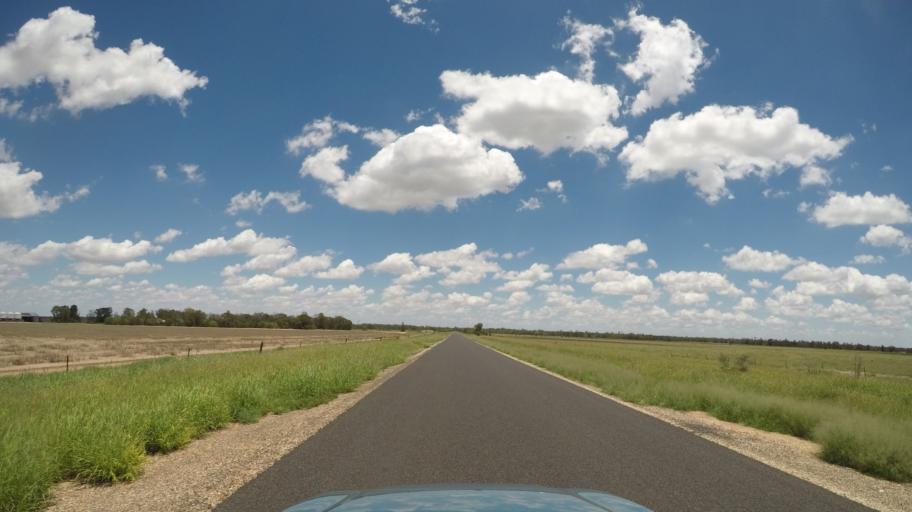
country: AU
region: Queensland
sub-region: Goondiwindi
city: Goondiwindi
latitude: -28.1610
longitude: 150.1373
